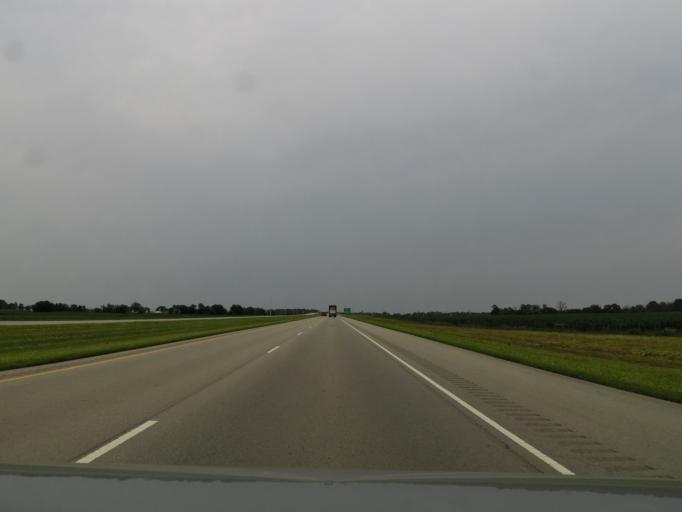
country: US
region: Ohio
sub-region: Clinton County
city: Wilmington
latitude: 39.4645
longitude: -83.8469
